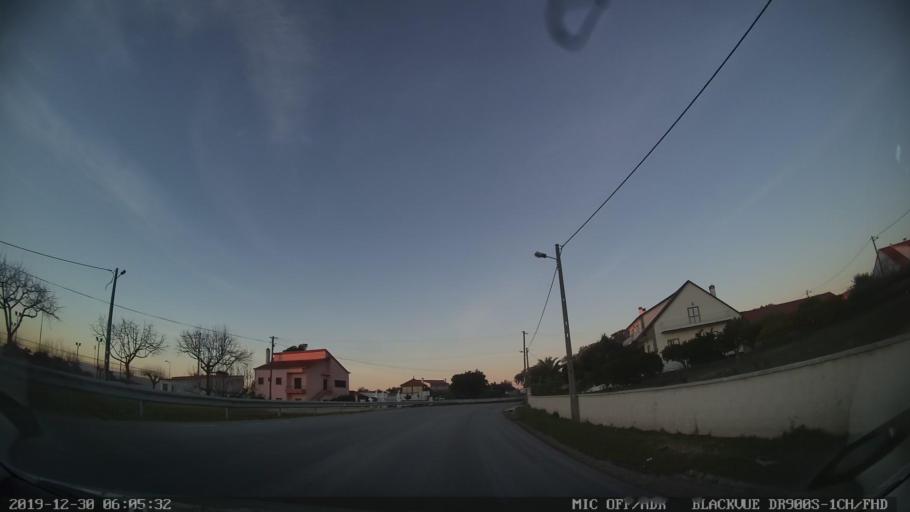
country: PT
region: Castelo Branco
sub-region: Penamacor
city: Penamacor
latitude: 40.0912
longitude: -7.2365
